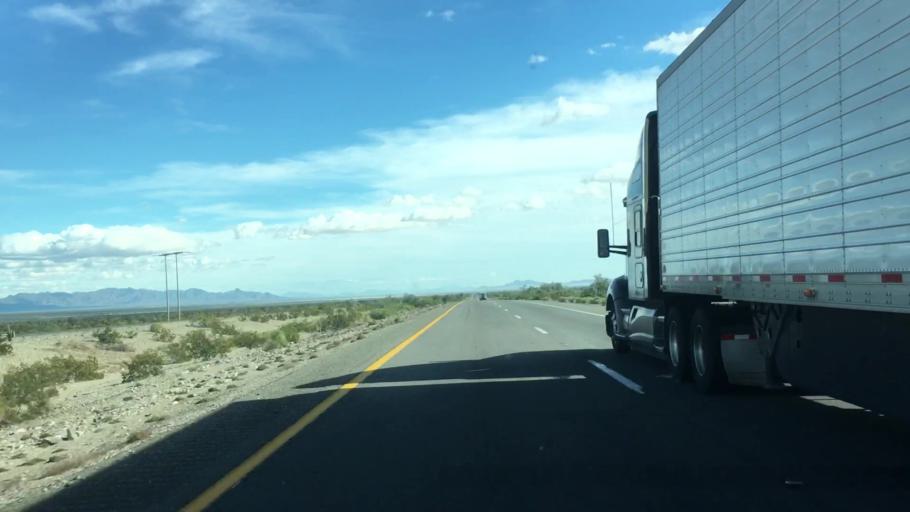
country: US
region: California
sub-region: Riverside County
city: Mesa Verde
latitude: 33.6772
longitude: -115.2266
